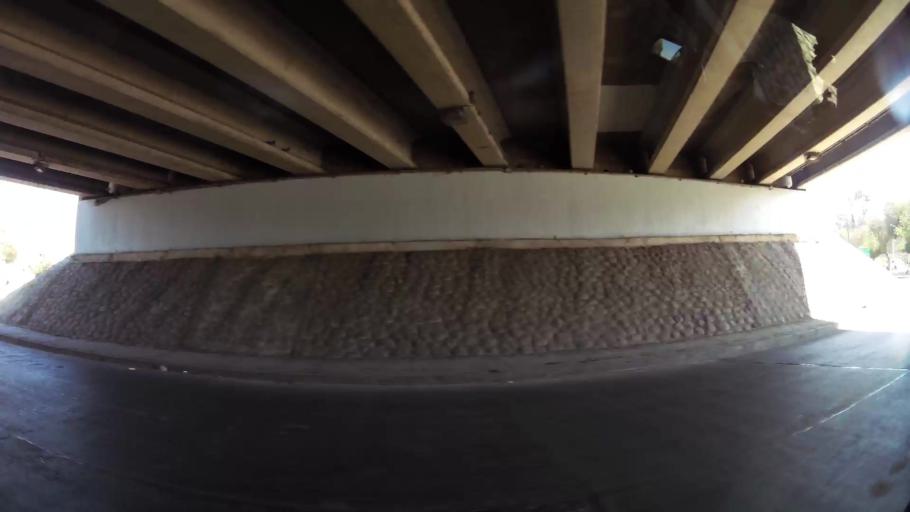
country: CL
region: Santiago Metropolitan
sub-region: Provincia de Santiago
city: Lo Prado
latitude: -33.4116
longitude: -70.7457
